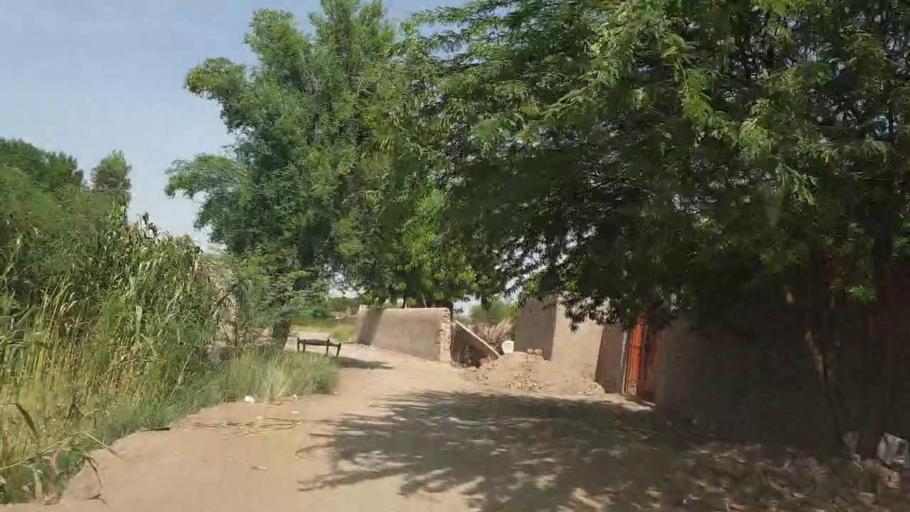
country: PK
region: Sindh
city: Bozdar
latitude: 27.0877
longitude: 68.6048
